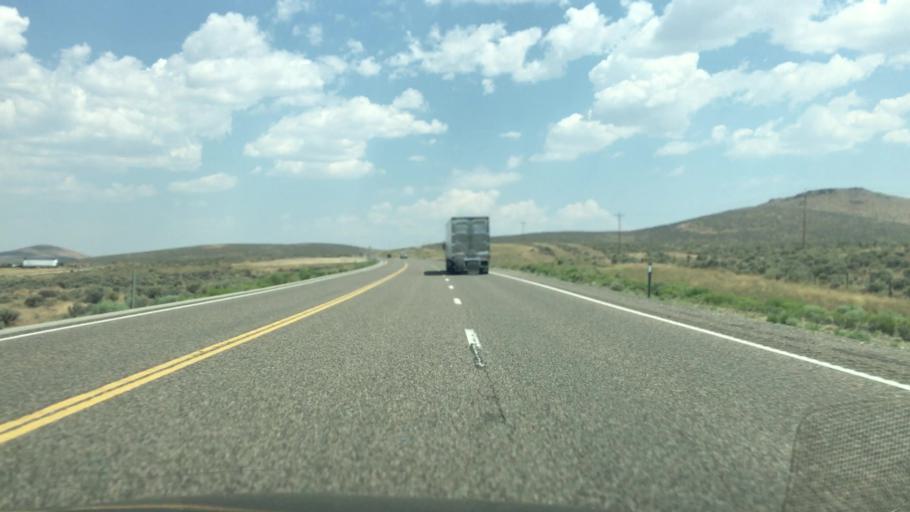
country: US
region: Nevada
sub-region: Elko County
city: Wells
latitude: 41.1761
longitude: -114.8786
